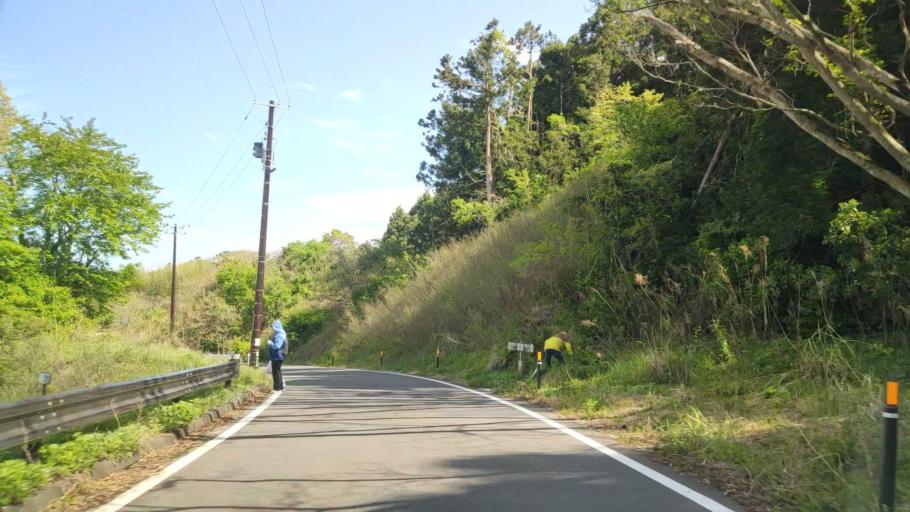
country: JP
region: Miyagi
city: Yamoto
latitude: 38.3358
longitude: 141.1607
